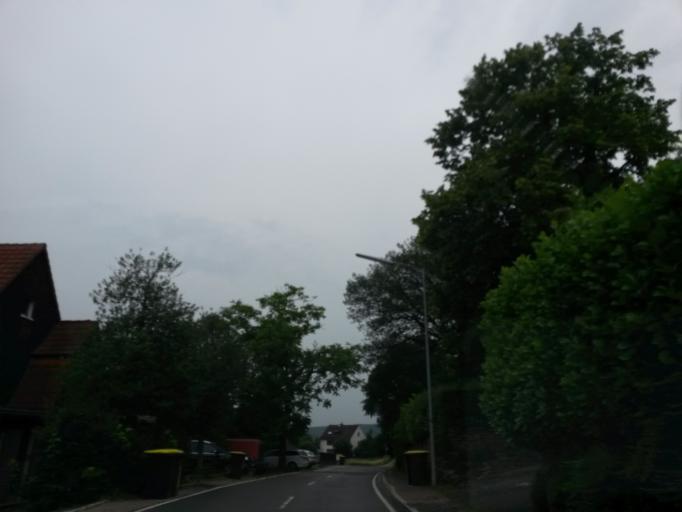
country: DE
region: North Rhine-Westphalia
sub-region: Regierungsbezirk Koln
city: Engelskirchen
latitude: 50.9586
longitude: 7.3627
